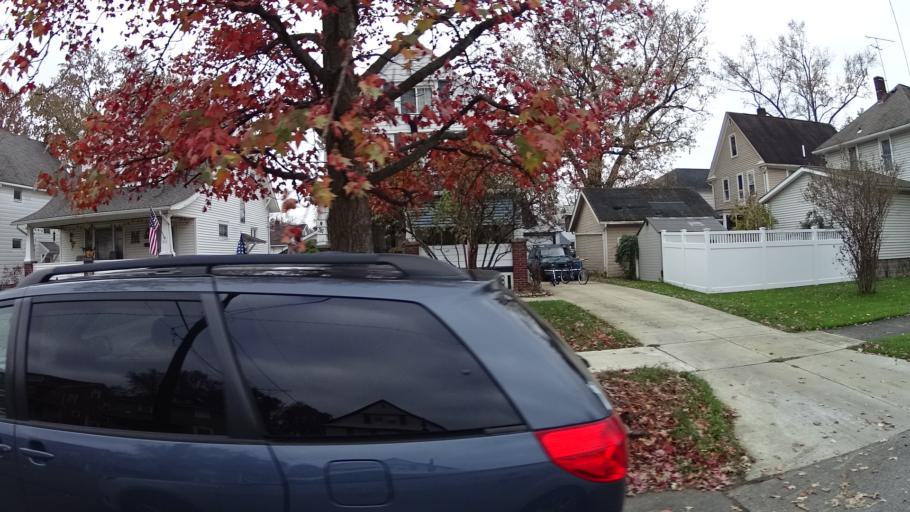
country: US
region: Ohio
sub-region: Lorain County
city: Elyria
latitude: 41.3641
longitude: -82.0942
